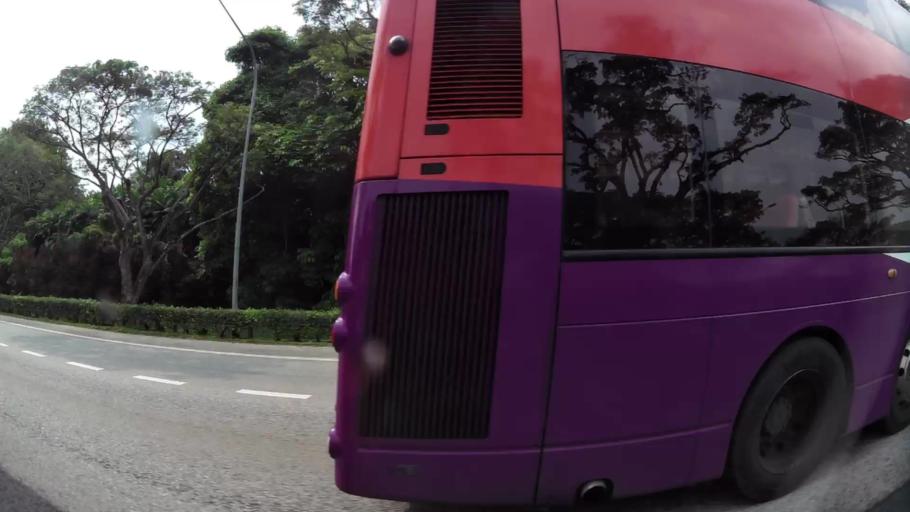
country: SG
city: Singapore
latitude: 1.3283
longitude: 103.9741
